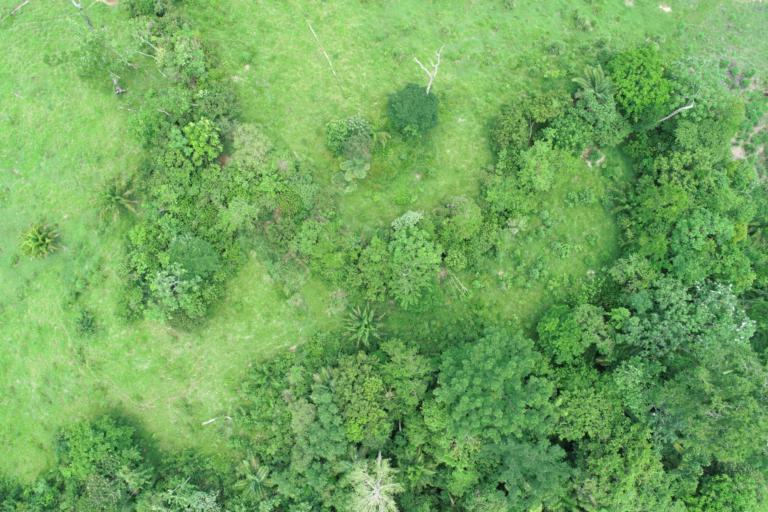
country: BO
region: El Beni
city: San Borja
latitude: -14.7441
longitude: -67.1638
